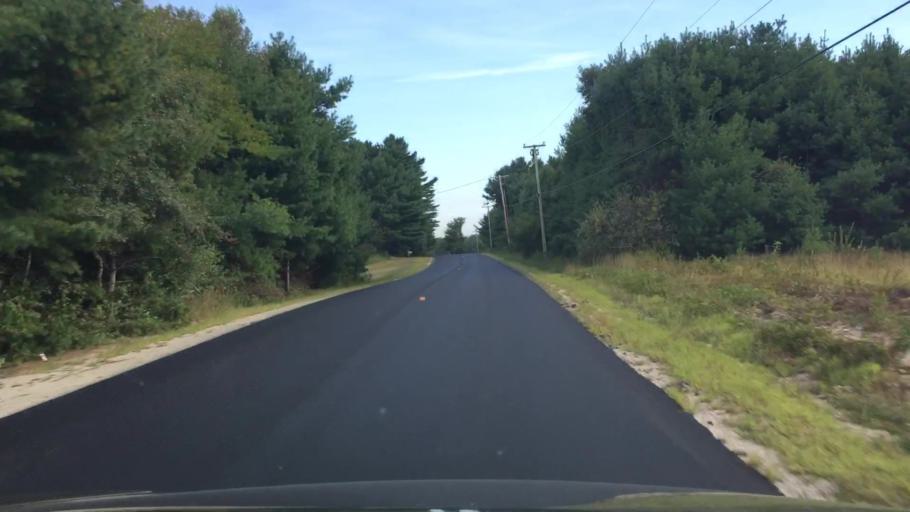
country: US
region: Maine
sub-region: Hancock County
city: Surry
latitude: 44.5299
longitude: -68.6123
